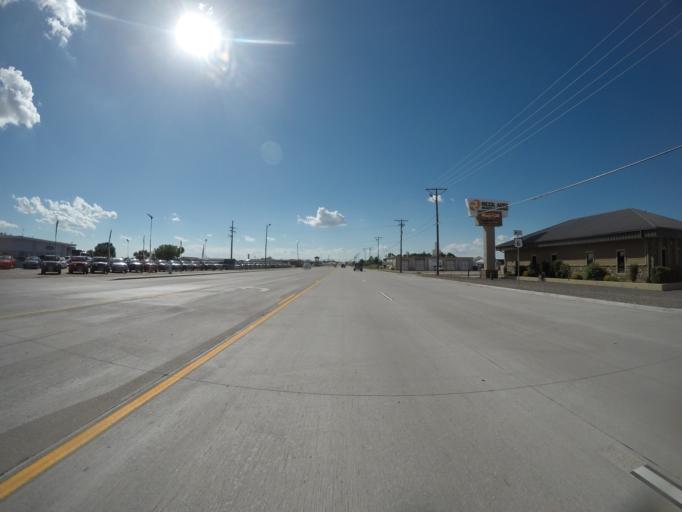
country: US
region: Colorado
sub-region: Logan County
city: Sterling
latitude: 40.6204
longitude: -103.1927
